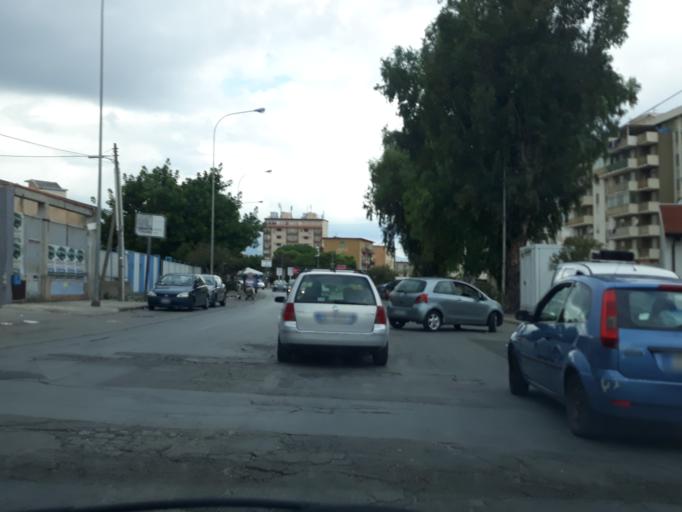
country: IT
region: Sicily
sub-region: Palermo
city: Ciaculli
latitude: 38.0967
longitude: 13.3941
